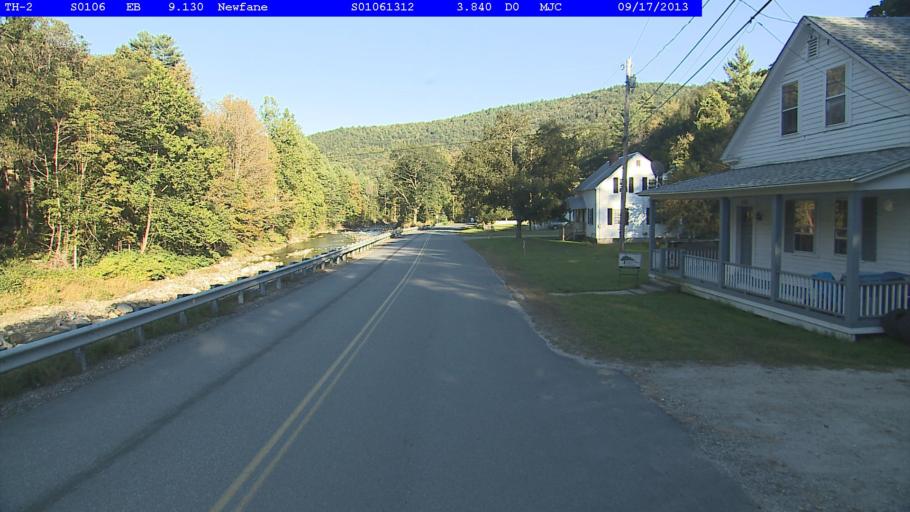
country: US
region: Vermont
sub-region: Windham County
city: Newfane
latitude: 42.9371
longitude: -72.7031
